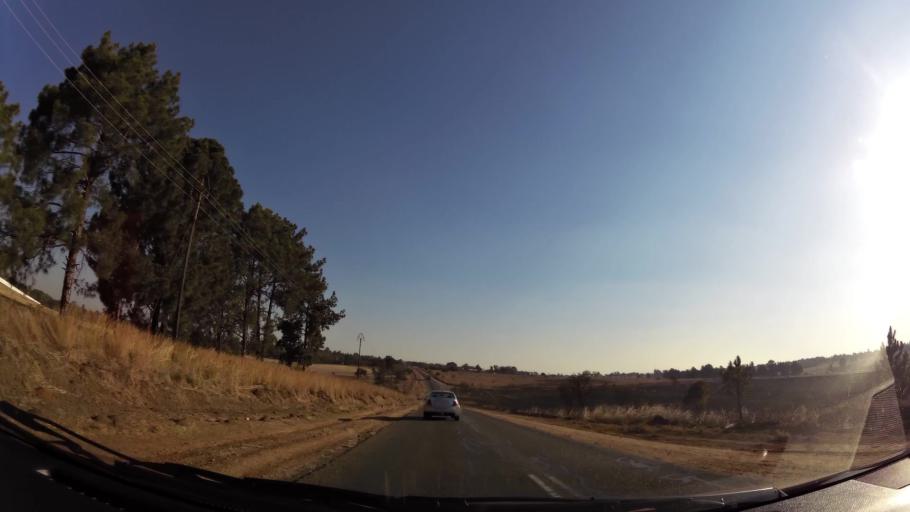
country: ZA
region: Gauteng
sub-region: West Rand District Municipality
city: Muldersdriseloop
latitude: -26.0077
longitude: 27.8982
